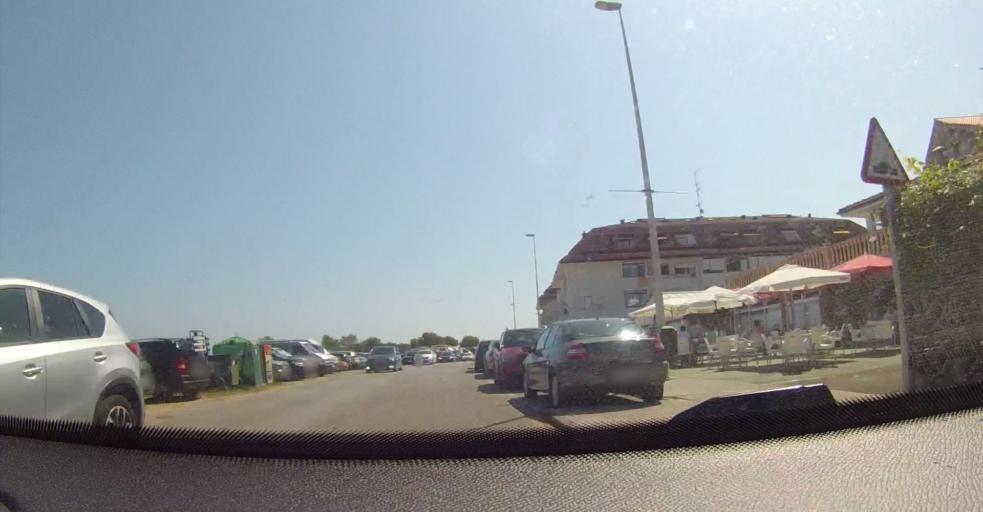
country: ES
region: Cantabria
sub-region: Provincia de Cantabria
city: Noja
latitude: 43.4724
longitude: -3.5081
